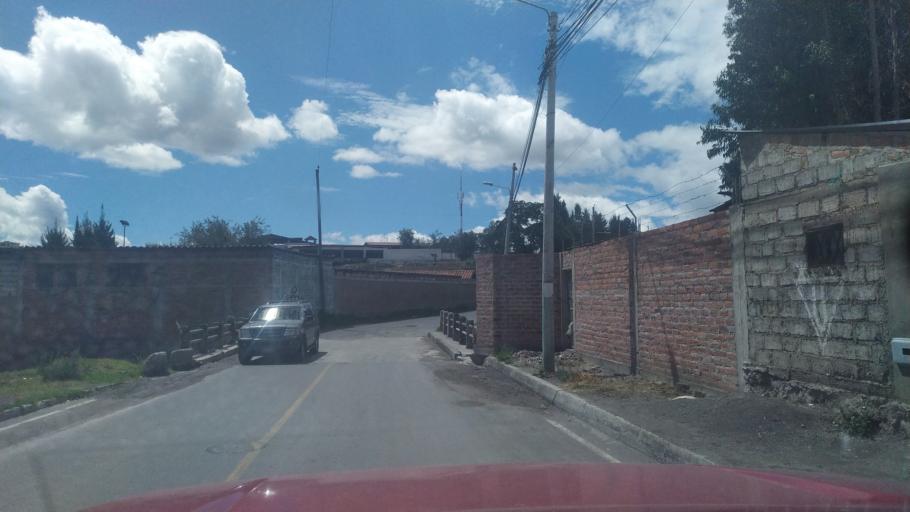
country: EC
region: Chimborazo
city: Riobamba
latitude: -1.6715
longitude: -78.6679
